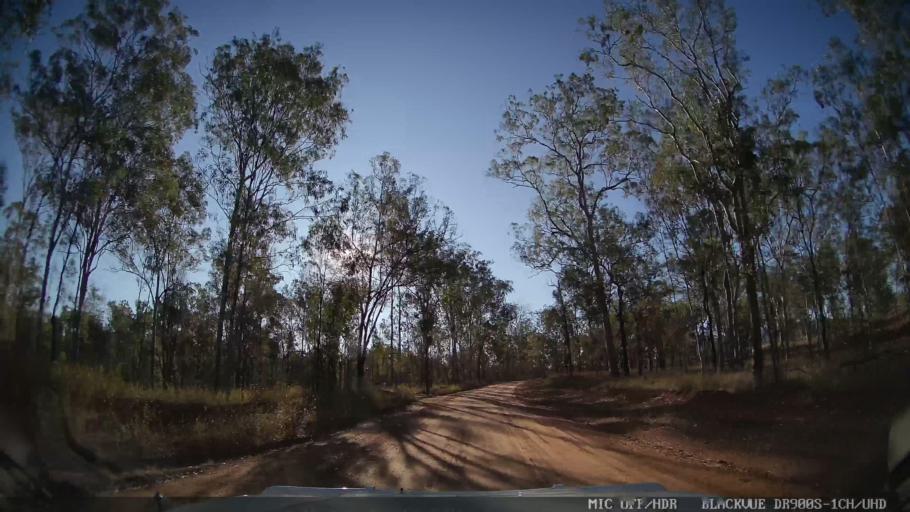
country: AU
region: Queensland
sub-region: Bundaberg
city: Sharon
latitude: -24.7387
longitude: 151.5241
